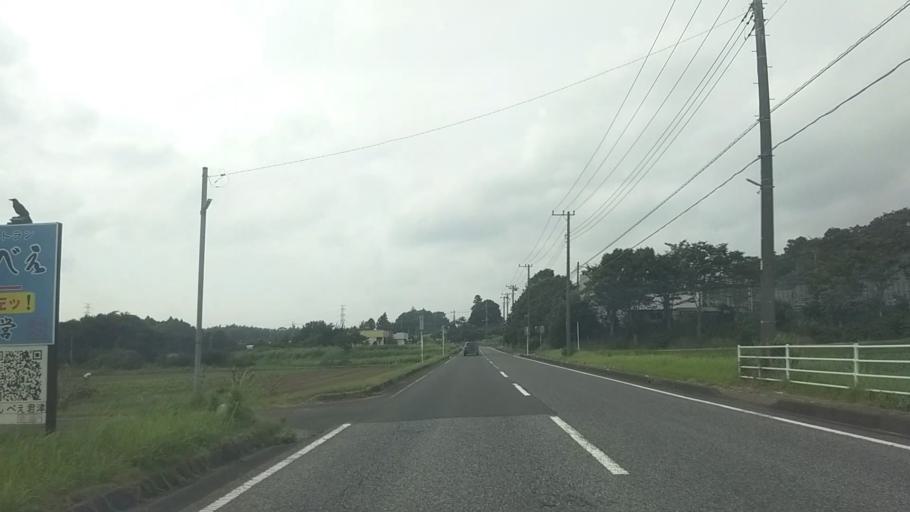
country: JP
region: Chiba
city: Kimitsu
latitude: 35.2751
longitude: 139.9945
